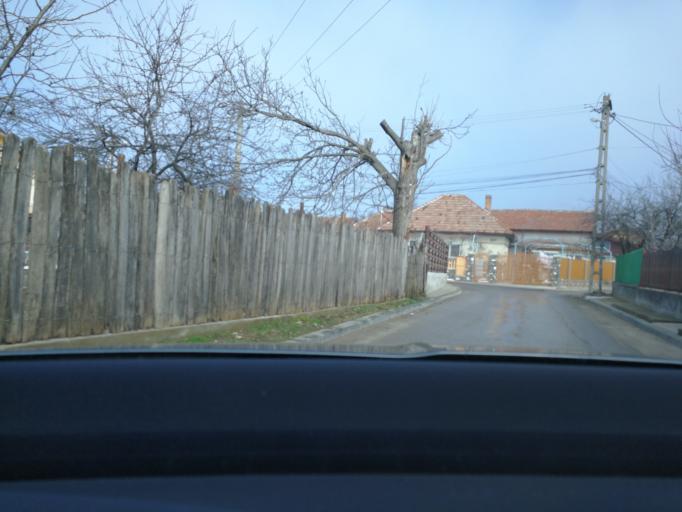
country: RO
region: Prahova
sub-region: Comuna Magureni
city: Lunca Prahovei
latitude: 45.0507
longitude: 25.7496
